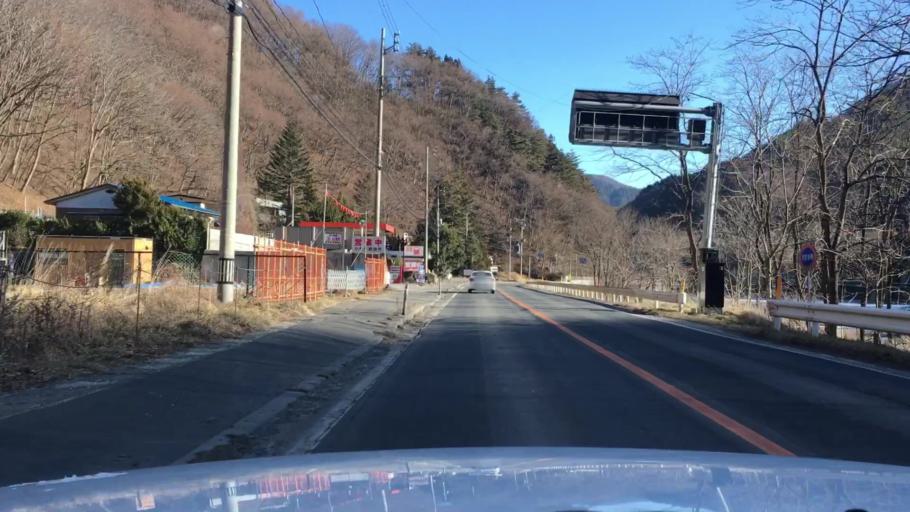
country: JP
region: Iwate
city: Miyako
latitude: 39.5919
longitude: 141.6710
